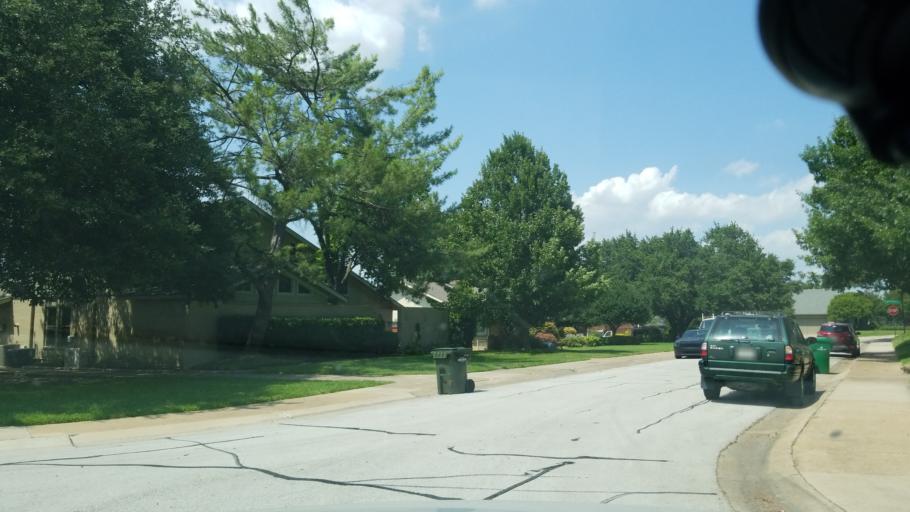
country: US
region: Texas
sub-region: Dallas County
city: Carrollton
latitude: 32.9597
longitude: -96.8605
